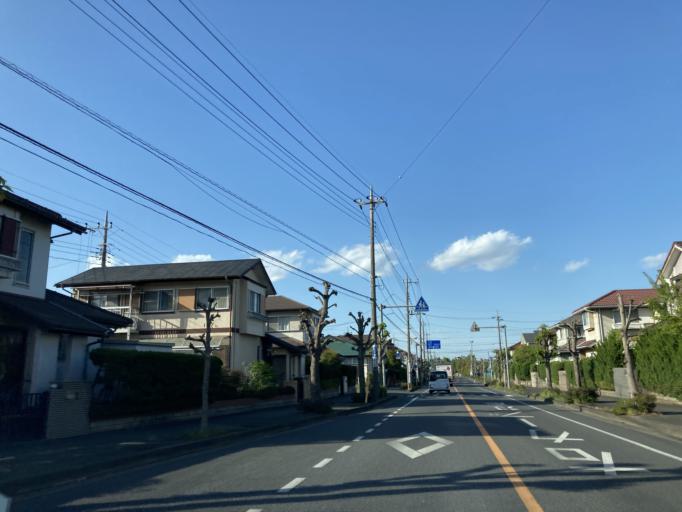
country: JP
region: Saitama
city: Sayama
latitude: 35.8853
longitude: 139.4141
